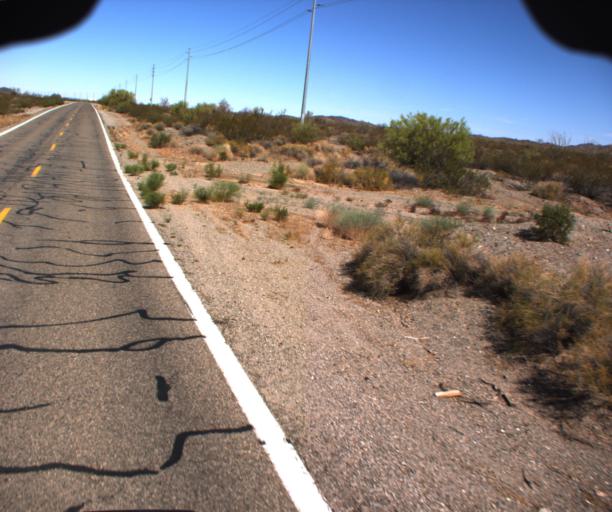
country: US
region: Arizona
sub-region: La Paz County
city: Salome
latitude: 33.7376
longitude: -113.7347
